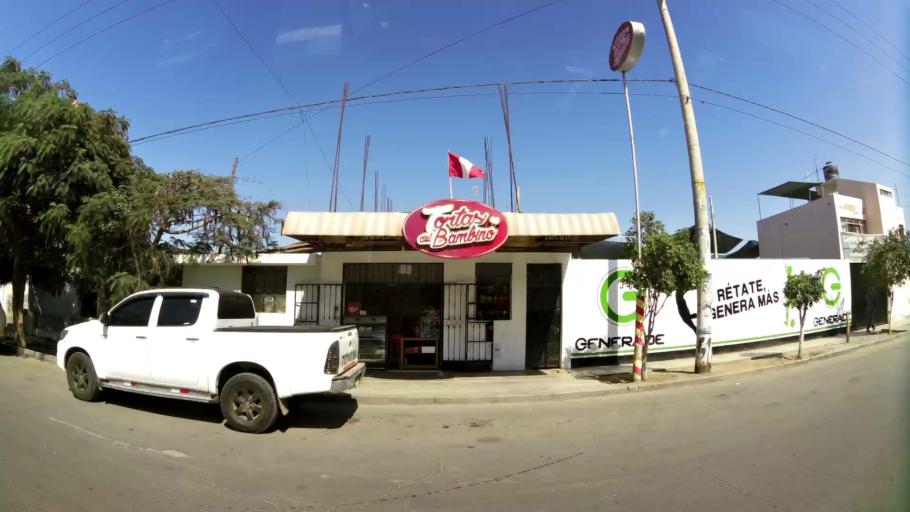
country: PE
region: Ica
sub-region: Provincia de Ica
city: La Tinguina
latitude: -14.0460
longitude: -75.7074
